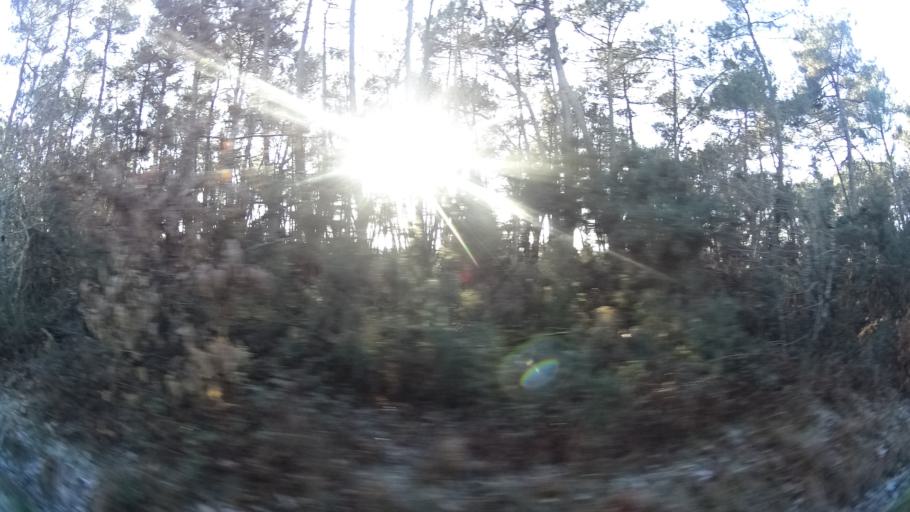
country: FR
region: Brittany
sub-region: Departement du Morbihan
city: Allaire
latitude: 47.6611
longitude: -2.1779
